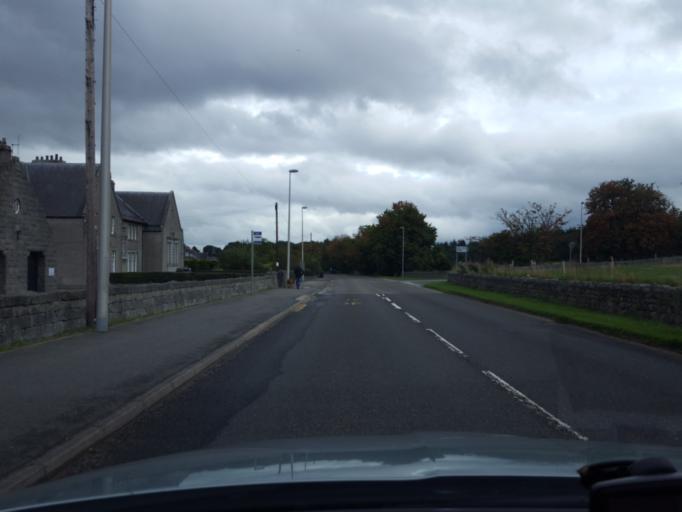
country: GB
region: Scotland
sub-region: Aberdeenshire
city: Kemnay
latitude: 57.1728
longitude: -2.4154
